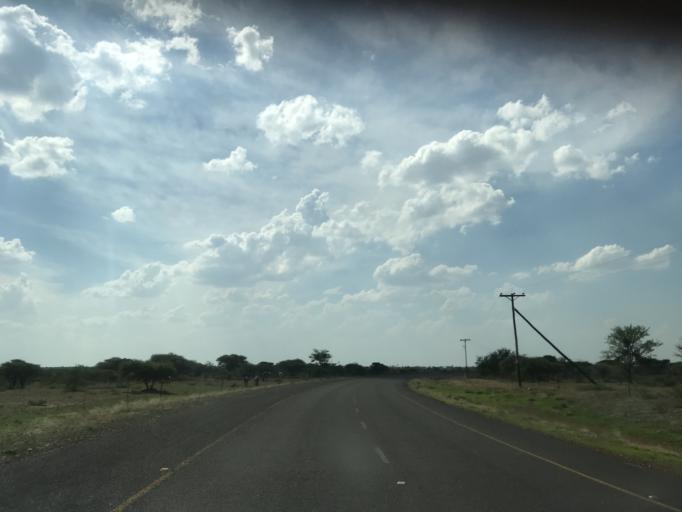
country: BW
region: South East
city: Janeng
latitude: -25.4913
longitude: 25.6280
